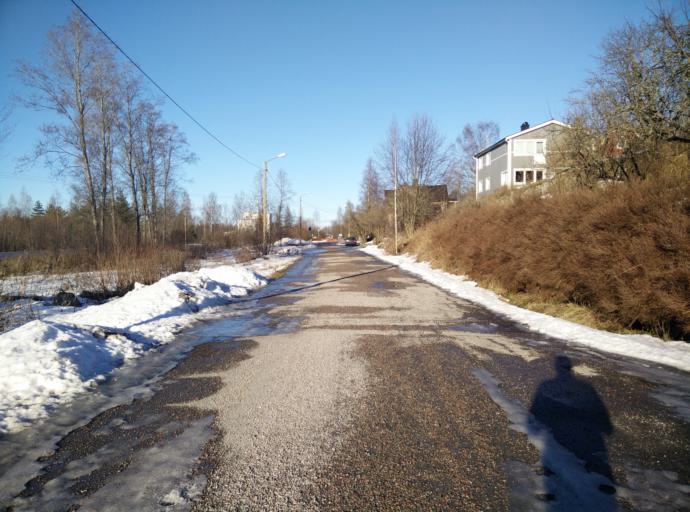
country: SE
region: Vaesternorrland
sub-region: Sundsvalls Kommun
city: Skottsund
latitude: 62.3045
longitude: 17.3849
